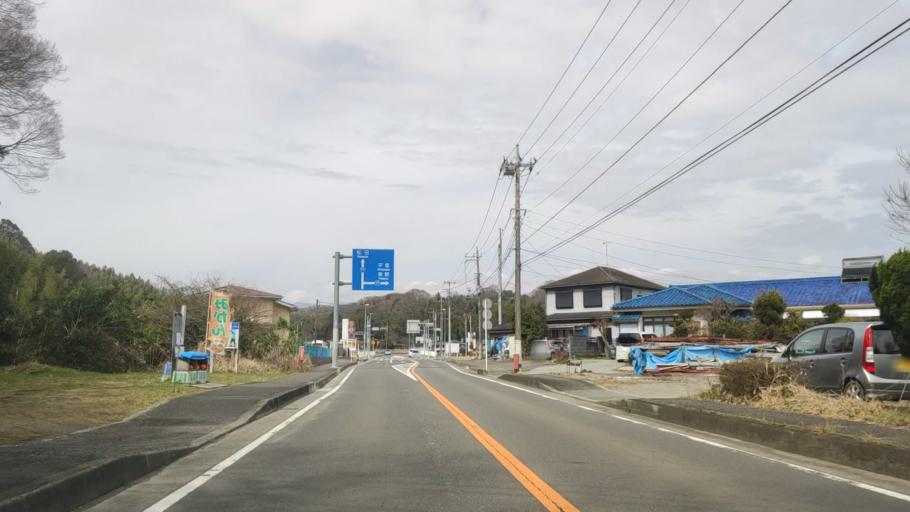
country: JP
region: Kanagawa
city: Hadano
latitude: 35.3294
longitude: 139.2173
